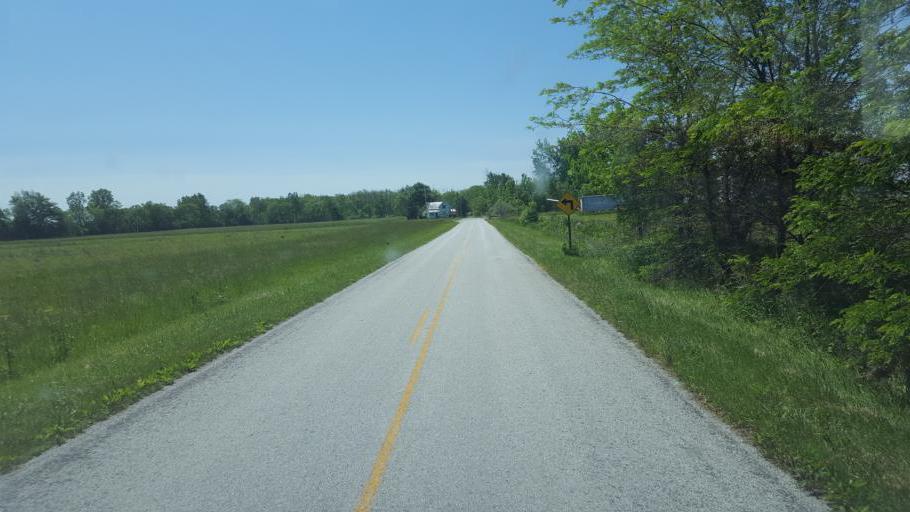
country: US
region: Ohio
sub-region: Hardin County
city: Kenton
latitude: 40.6091
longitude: -83.4203
